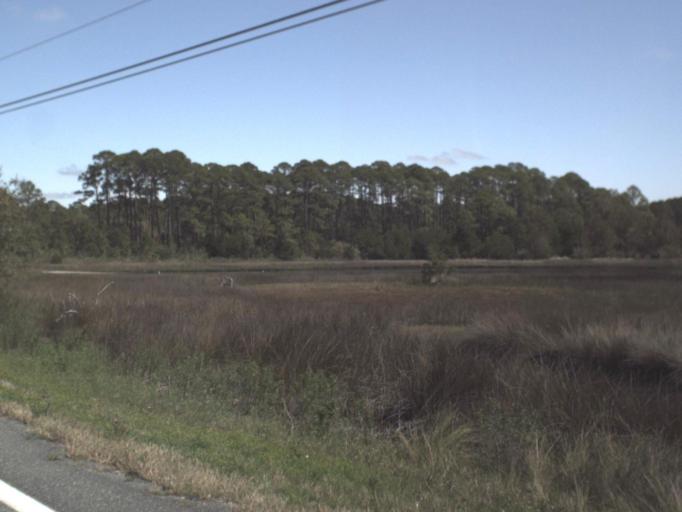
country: US
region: Florida
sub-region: Wakulla County
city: Crawfordville
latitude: 30.0148
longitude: -84.3931
